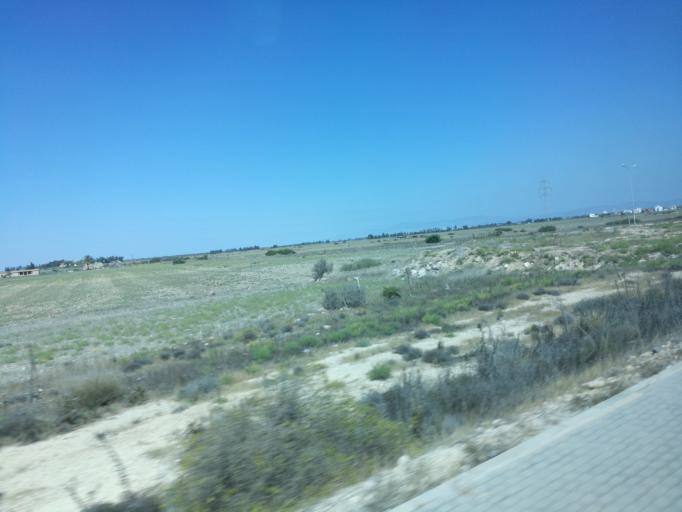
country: CY
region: Ammochostos
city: Famagusta
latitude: 35.1775
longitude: 33.8963
